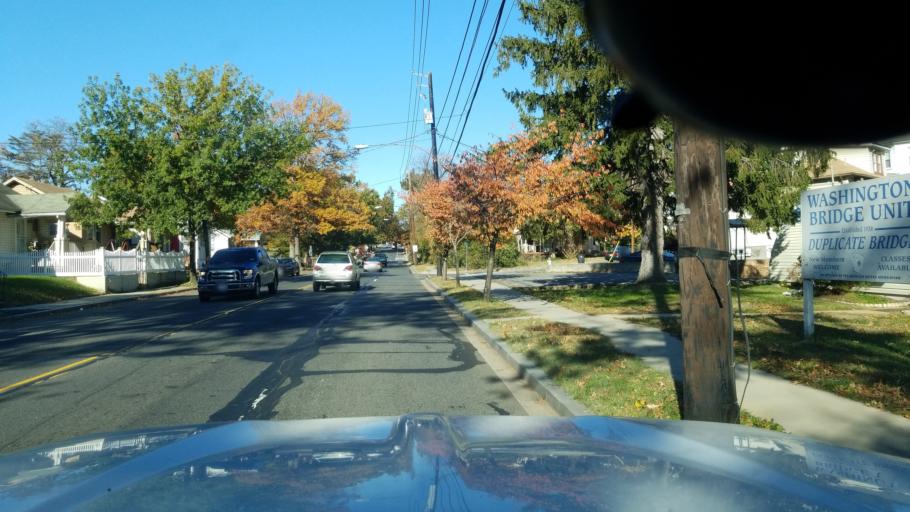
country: US
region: Maryland
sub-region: Prince George's County
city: Mount Rainier
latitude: 38.9368
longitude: -76.9654
